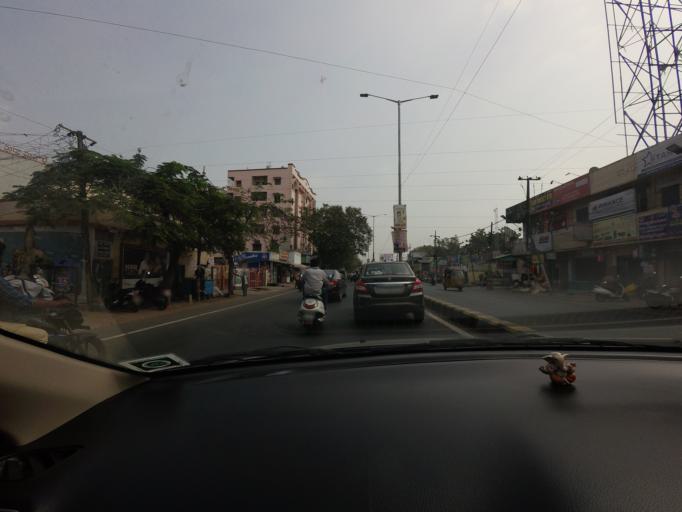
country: IN
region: Andhra Pradesh
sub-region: Krishna
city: Yanamalakuduru
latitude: 16.4936
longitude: 80.6642
